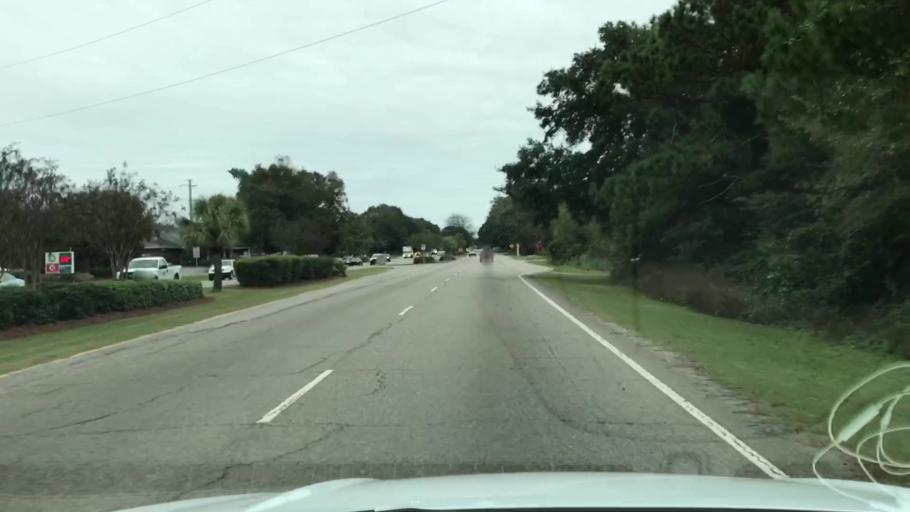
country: US
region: South Carolina
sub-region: Georgetown County
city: Murrells Inlet
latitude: 33.4795
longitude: -79.0996
